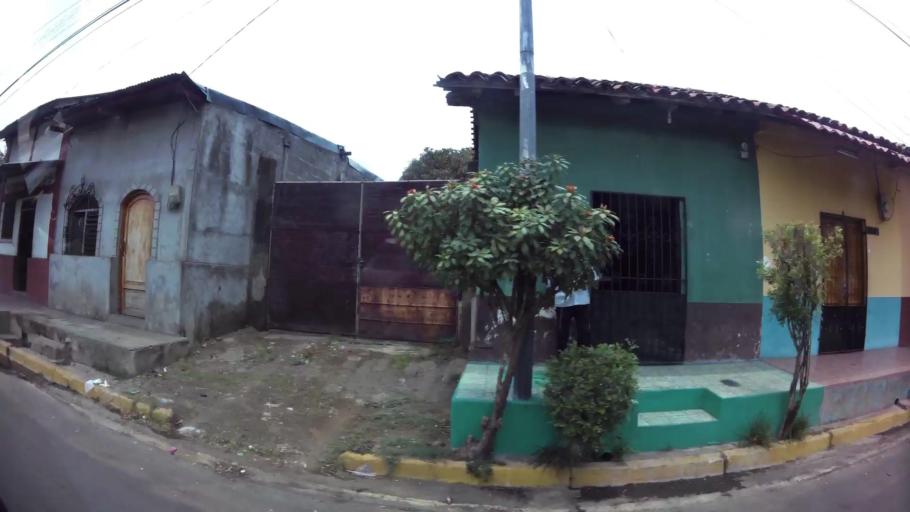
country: NI
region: Leon
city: Leon
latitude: 12.4316
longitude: -86.8881
